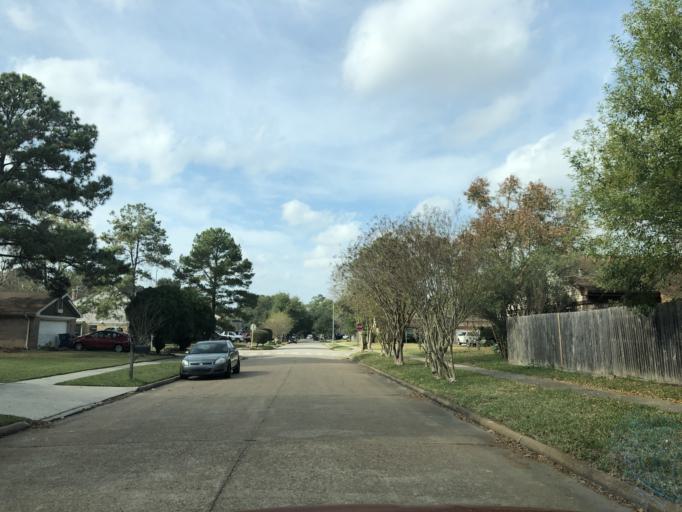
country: US
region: Texas
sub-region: Harris County
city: Tomball
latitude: 30.0357
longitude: -95.5415
